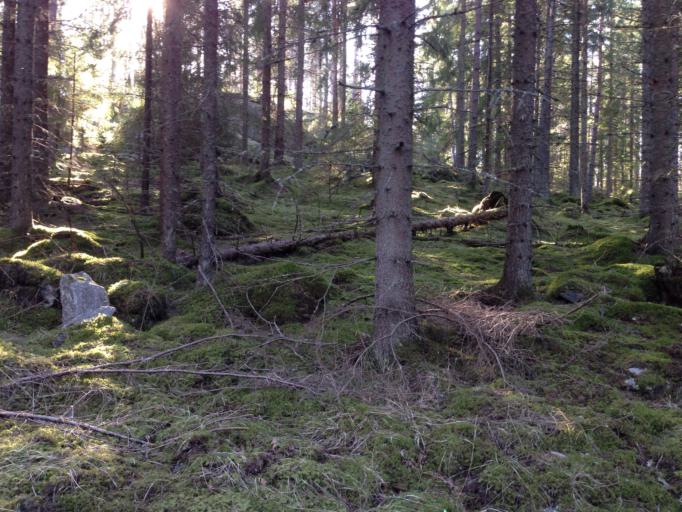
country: SE
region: OErebro
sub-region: Orebro Kommun
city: Odensbacken
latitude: 58.9727
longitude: 15.6424
